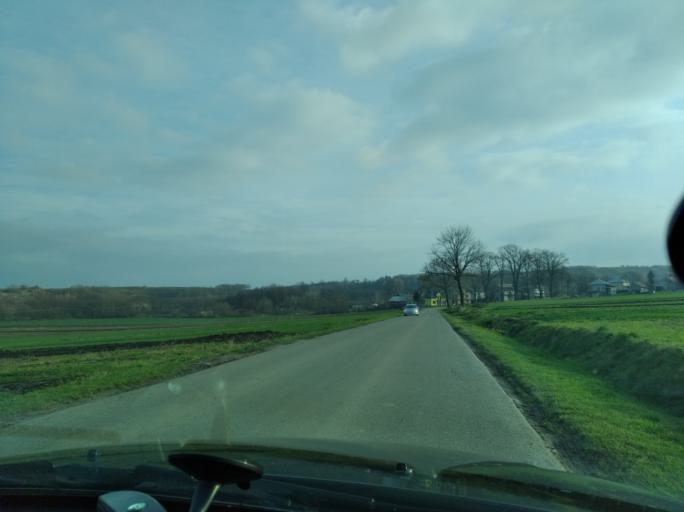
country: PL
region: Subcarpathian Voivodeship
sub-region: Powiat przeworski
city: Lopuszka Wielka
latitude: 49.9542
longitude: 22.4063
